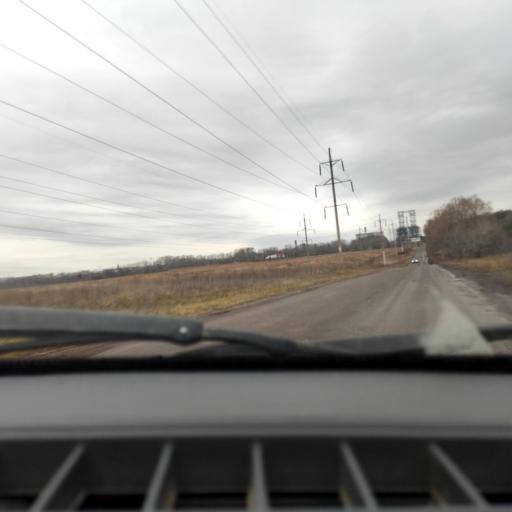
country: RU
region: Bashkortostan
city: Blagoveshchensk
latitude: 54.9398
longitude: 56.0930
